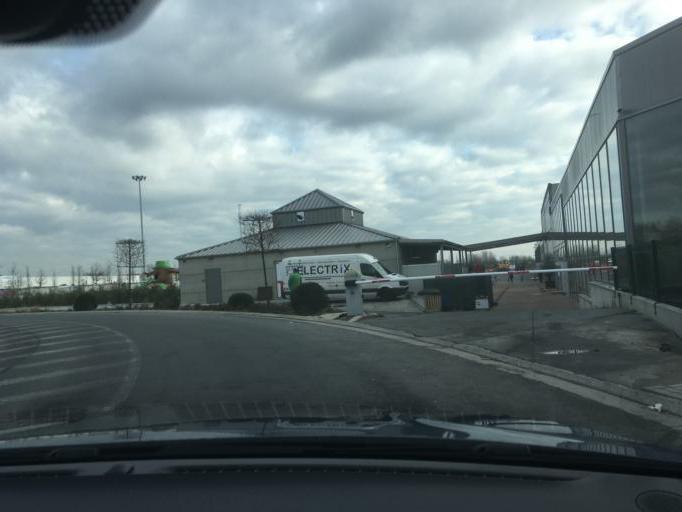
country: BE
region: Wallonia
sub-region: Province du Hainaut
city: Estaimpuis
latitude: 50.7177
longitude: 3.2822
